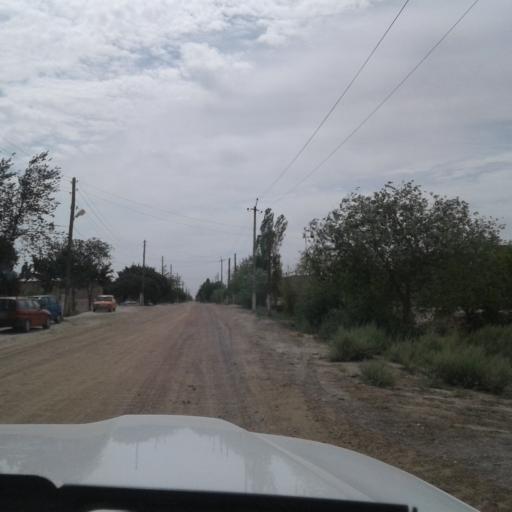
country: TM
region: Dasoguz
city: Tagta
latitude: 41.6026
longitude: 59.8458
